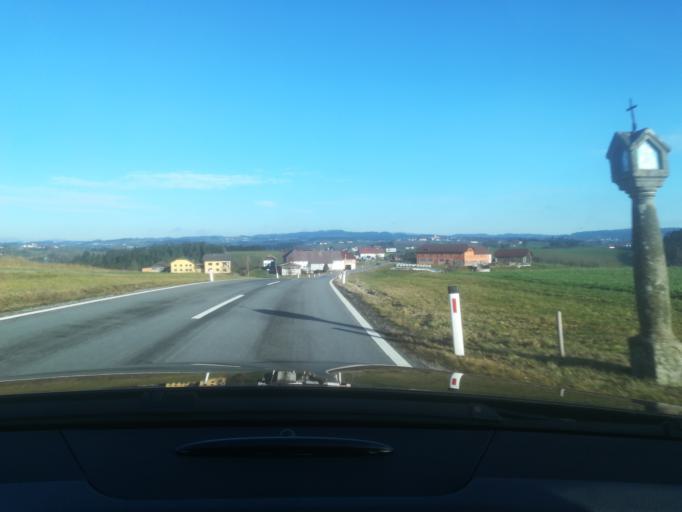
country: AT
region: Upper Austria
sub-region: Politischer Bezirk Urfahr-Umgebung
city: Herzogsdorf
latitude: 48.4124
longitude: 14.0881
